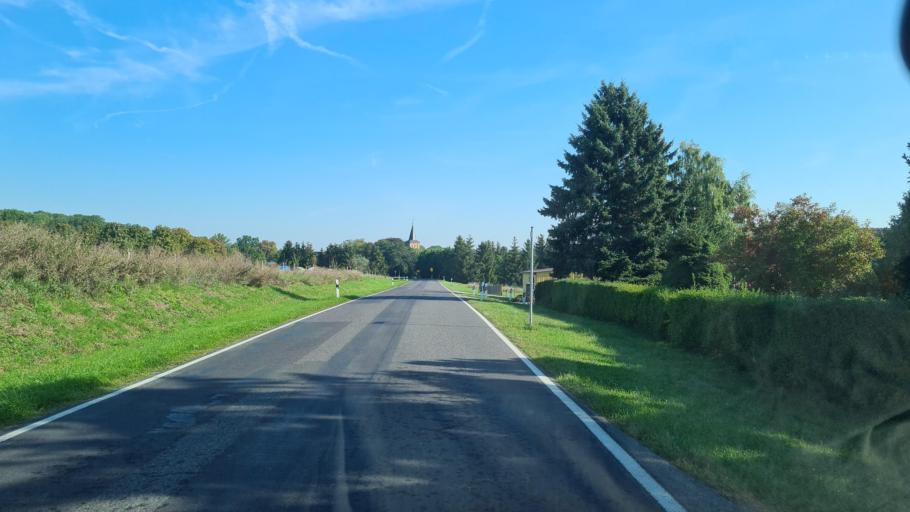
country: DE
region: Brandenburg
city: Pessin
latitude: 52.6872
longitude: 12.6483
